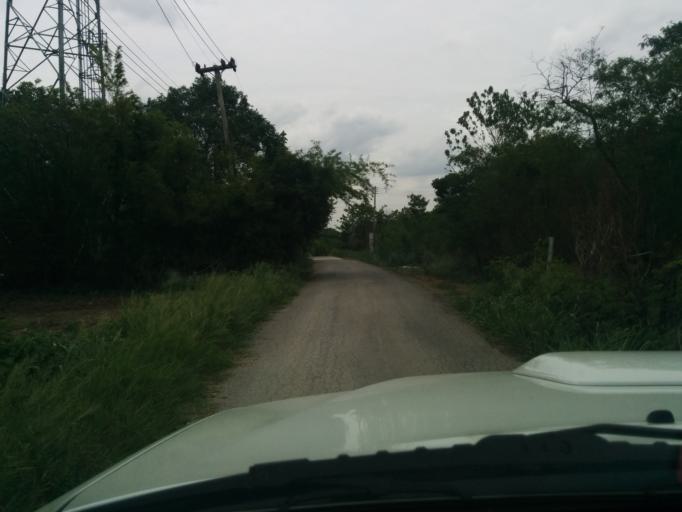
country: TH
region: Sara Buri
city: Muak Lek
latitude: 14.6173
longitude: 101.2084
